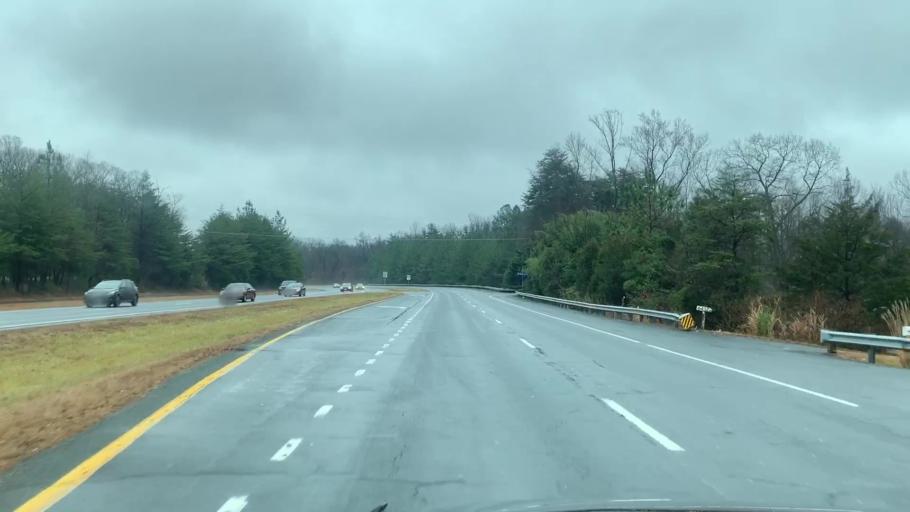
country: US
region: Virginia
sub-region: Fairfax County
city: Fairfax Station
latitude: 38.7791
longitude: -77.3271
